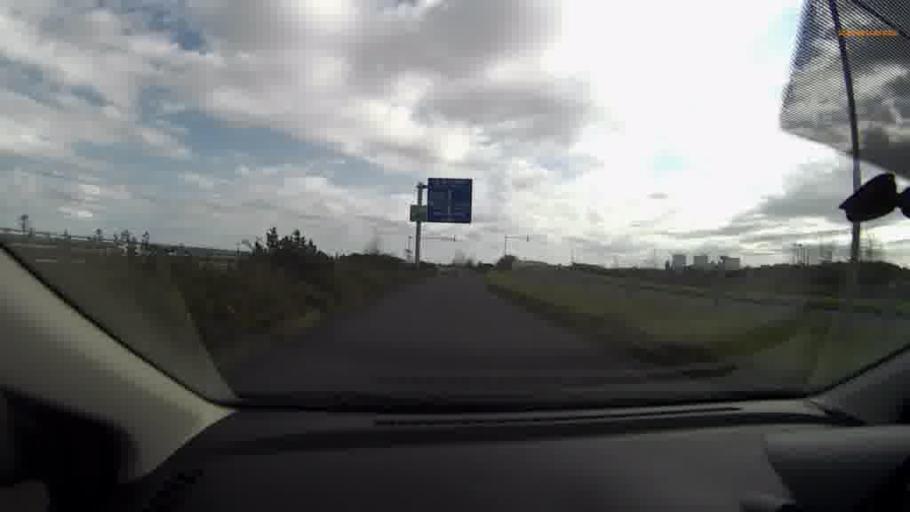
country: JP
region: Hokkaido
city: Kushiro
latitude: 43.0203
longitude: 144.2593
